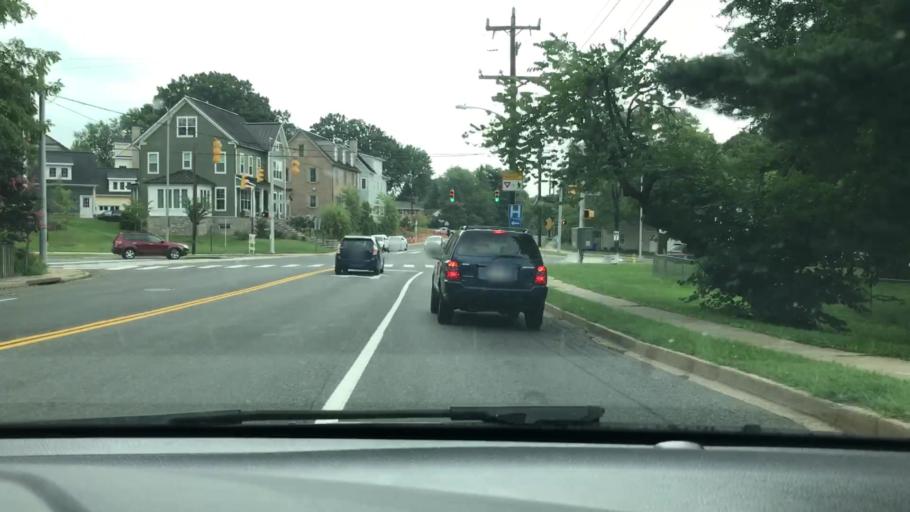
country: US
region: Virginia
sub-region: Arlington County
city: Arlington
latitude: 38.8849
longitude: -77.1274
